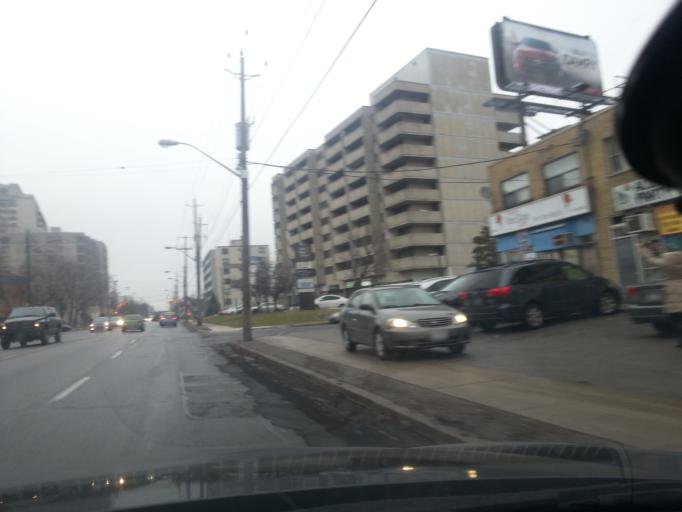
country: CA
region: Ontario
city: Toronto
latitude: 43.7300
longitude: -79.4322
